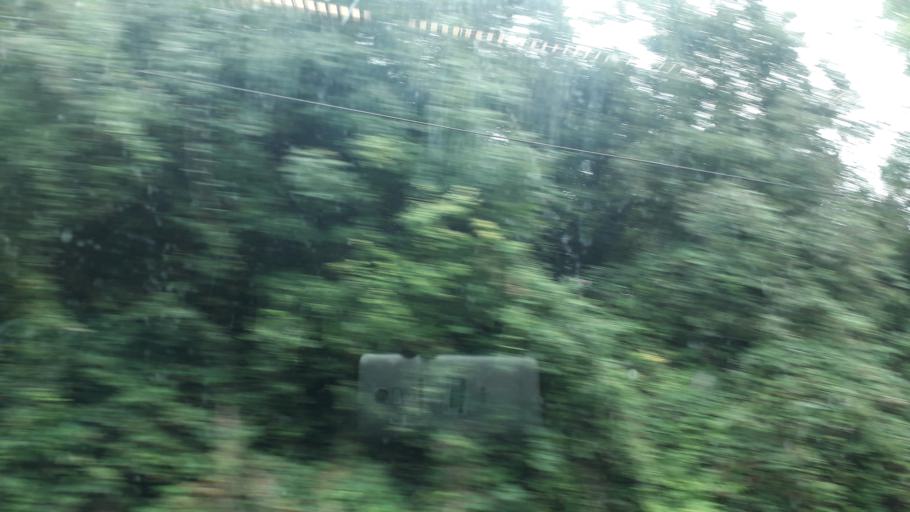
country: IE
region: Leinster
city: Malahide
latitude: 53.4407
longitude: -6.1562
